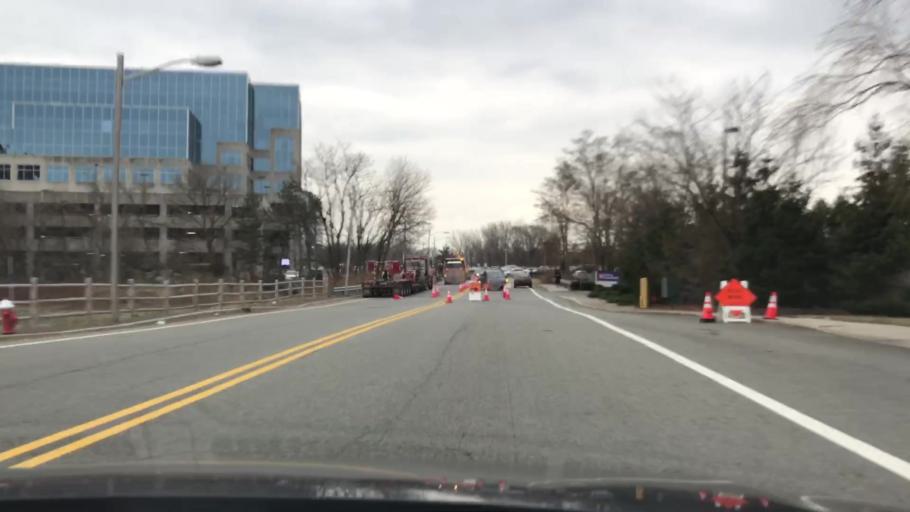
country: US
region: New Jersey
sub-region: Bergen County
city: Ridgefield Park
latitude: 40.8521
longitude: -74.0124
